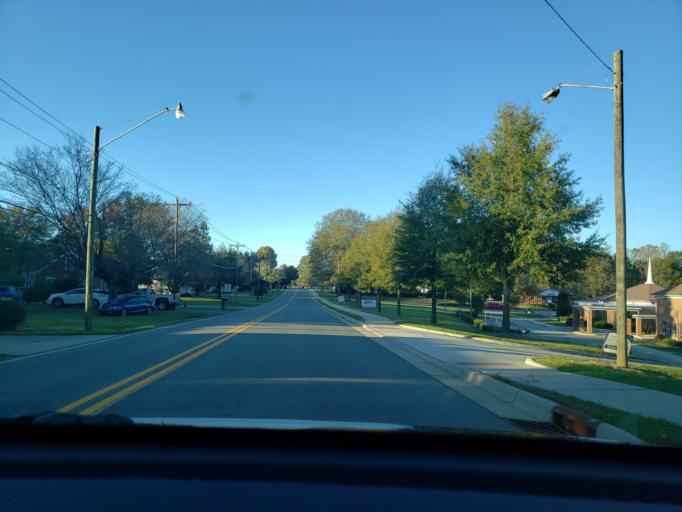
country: US
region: North Carolina
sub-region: Forsyth County
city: Walkertown
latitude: 36.1624
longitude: -80.1465
